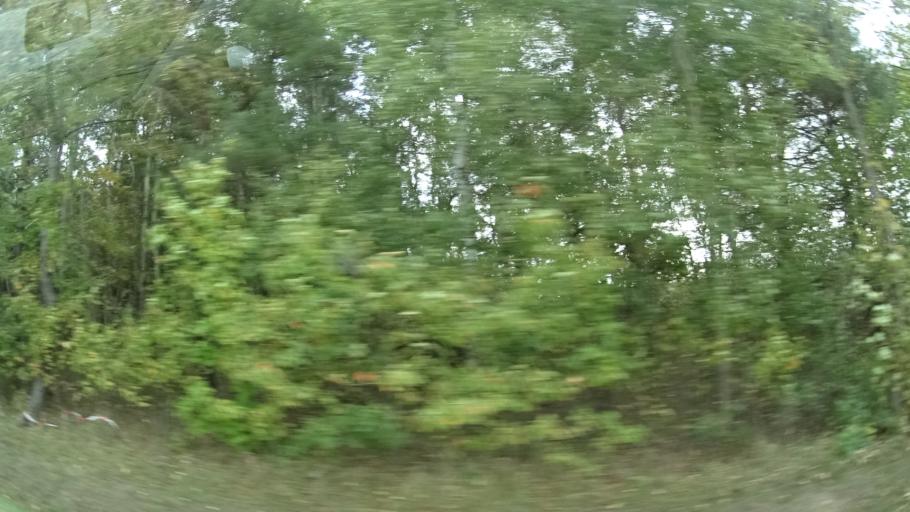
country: DE
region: Thuringia
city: Schwallungen
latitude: 50.7061
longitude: 10.3636
